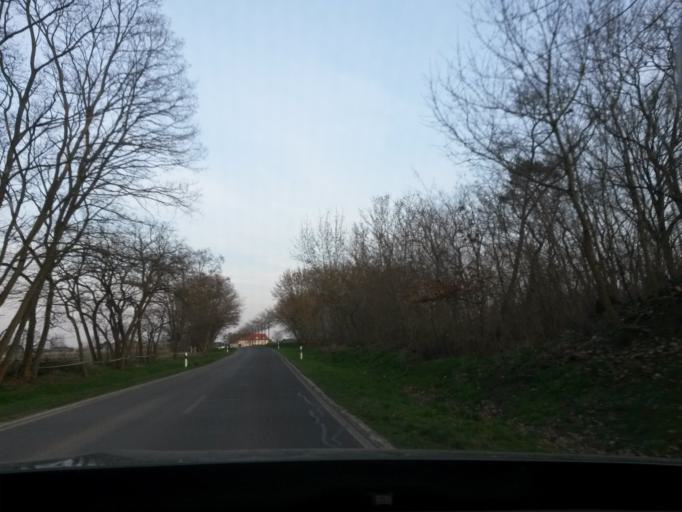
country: DE
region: Brandenburg
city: Strausberg
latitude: 52.5955
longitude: 13.9422
